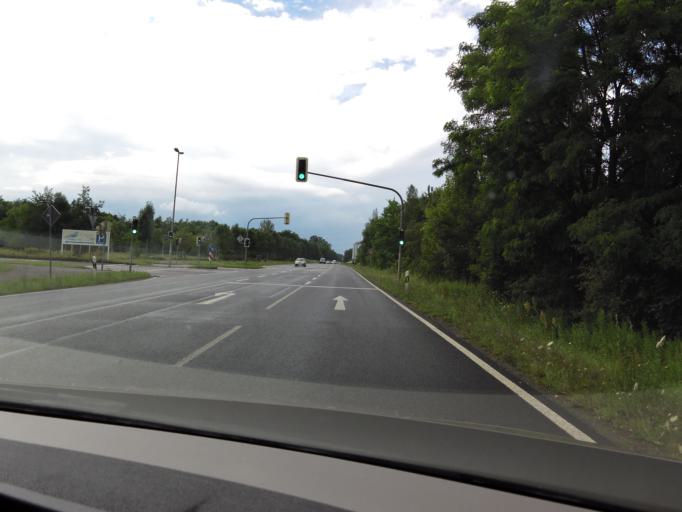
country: DE
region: Saxony
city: Markkleeberg
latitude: 51.2928
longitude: 12.3542
